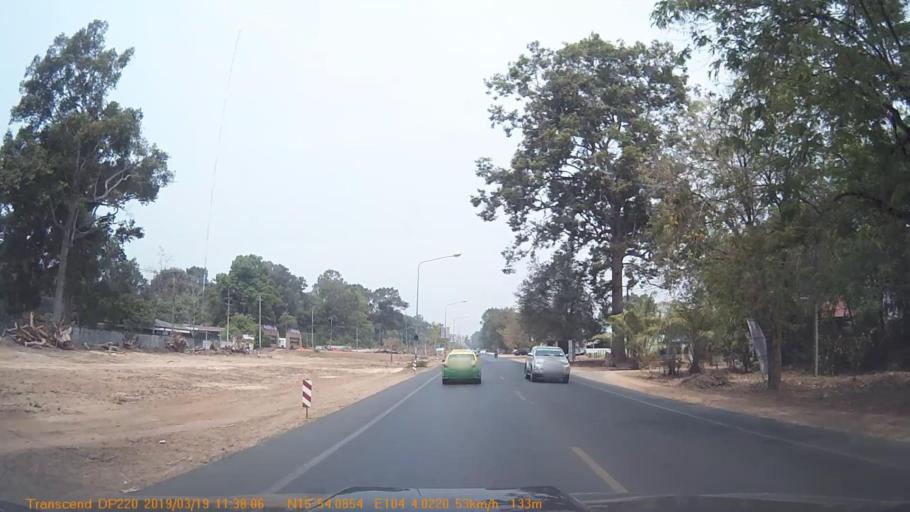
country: TH
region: Yasothon
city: Yasothon
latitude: 15.9015
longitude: 104.0670
